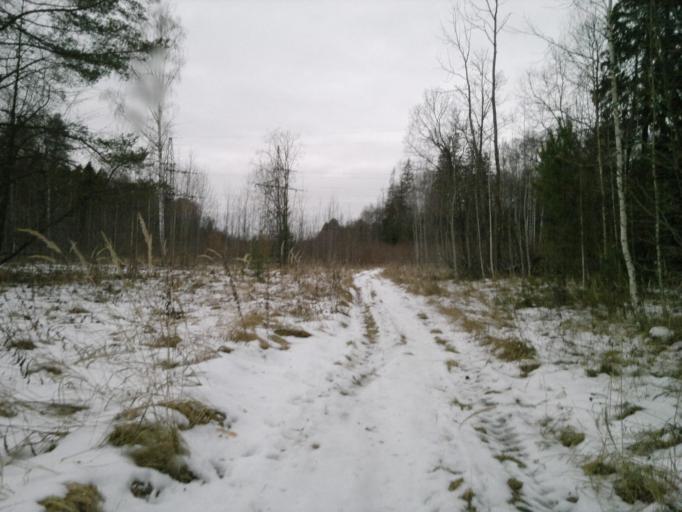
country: RU
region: Mariy-El
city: Yoshkar-Ola
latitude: 56.6040
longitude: 47.9578
